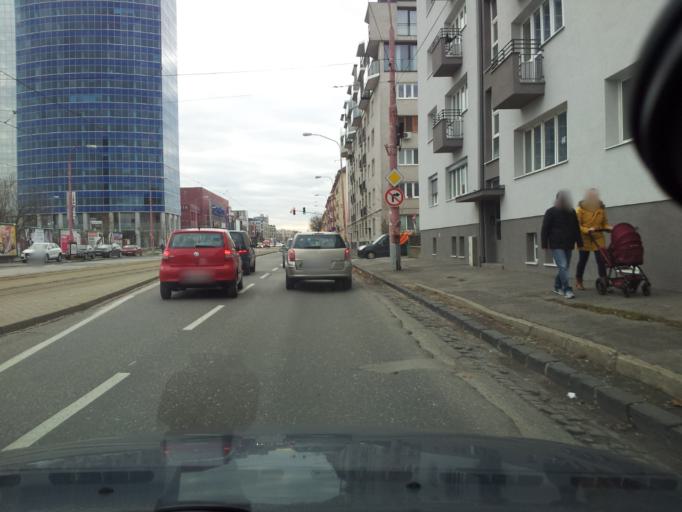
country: SK
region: Bratislavsky
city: Bratislava
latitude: 48.1716
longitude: 17.1408
